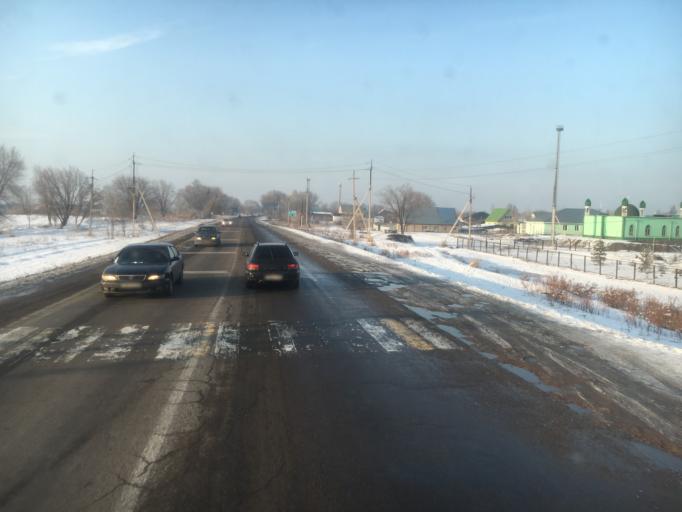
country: KZ
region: Almaty Oblysy
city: Burunday
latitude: 43.3325
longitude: 76.6616
